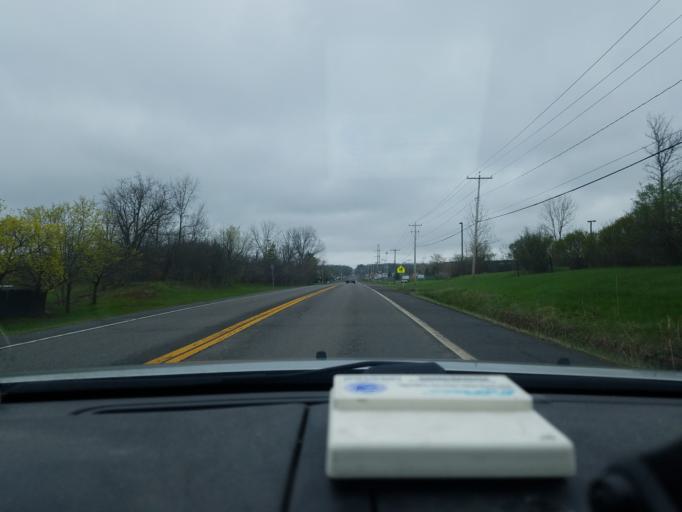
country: US
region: New York
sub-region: Onondaga County
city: North Syracuse
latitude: 43.1596
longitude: -76.0992
